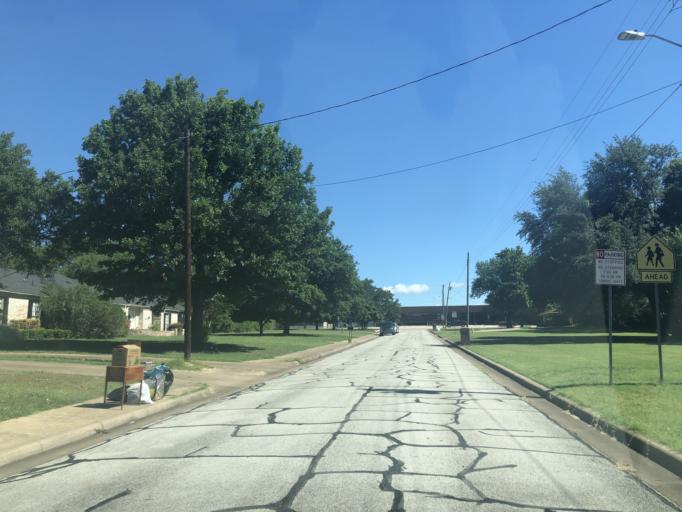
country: US
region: Texas
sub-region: Dallas County
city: Duncanville
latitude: 32.6378
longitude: -96.9315
